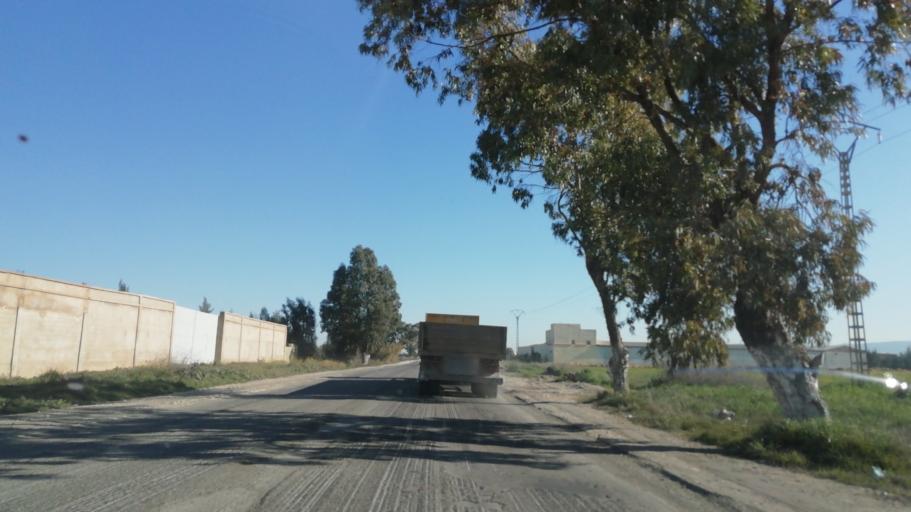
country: DZ
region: Relizane
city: Zemoura
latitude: 35.7554
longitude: 0.6774
